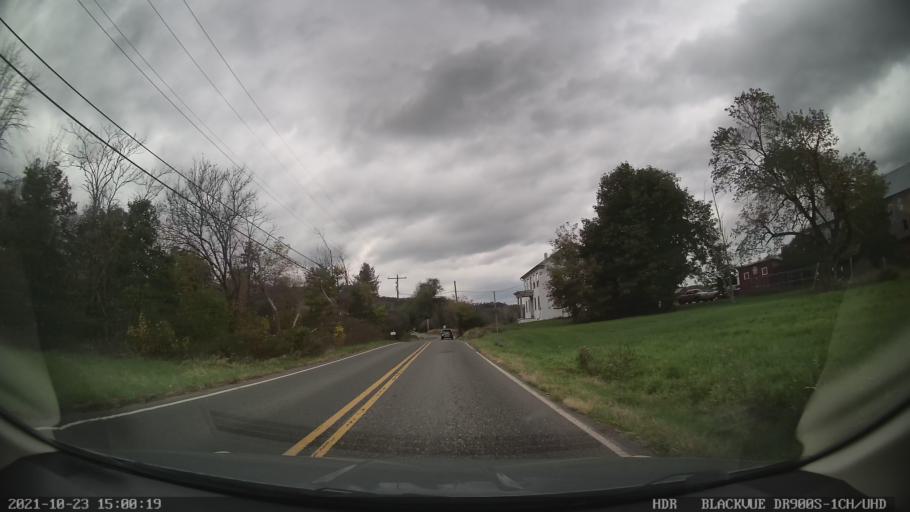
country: US
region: Pennsylvania
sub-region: Montgomery County
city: East Greenville
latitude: 40.3971
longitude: -75.5368
